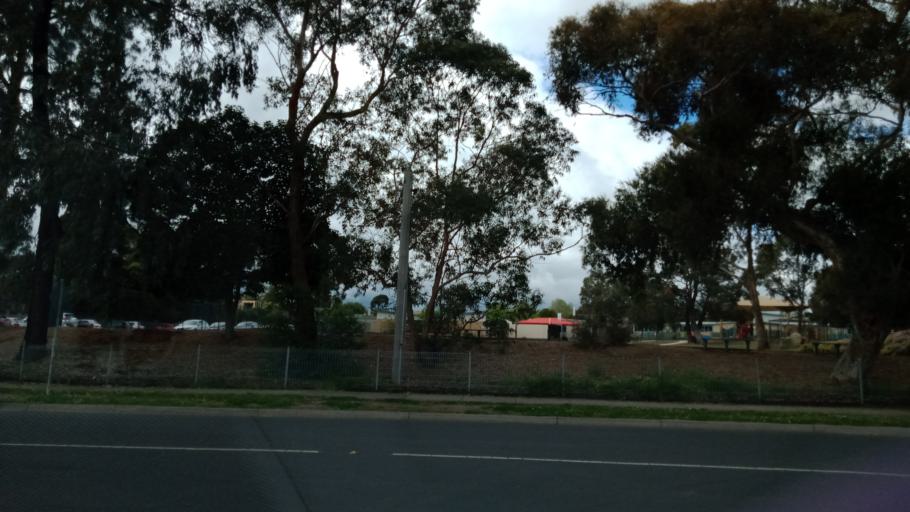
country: AU
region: Victoria
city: Burwood East
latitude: -37.8661
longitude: 145.1567
